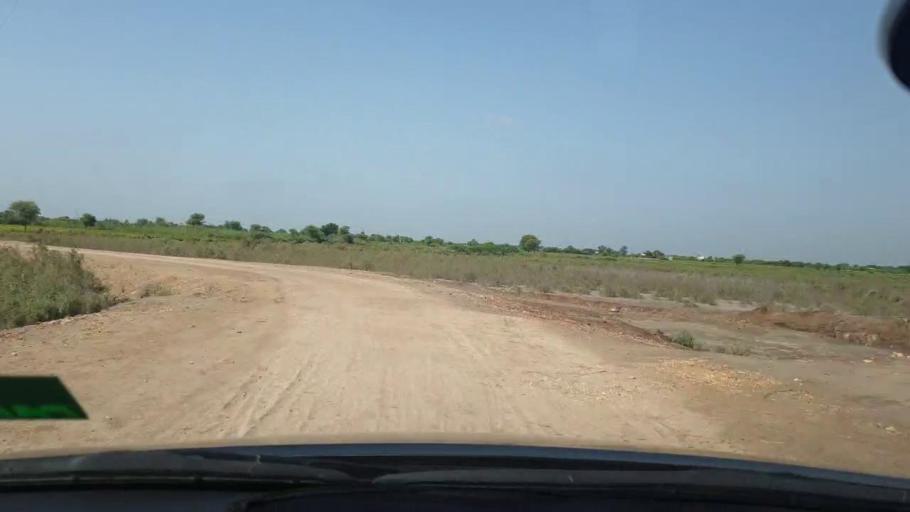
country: PK
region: Sindh
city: Tando Bago
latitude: 24.7401
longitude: 68.9700
